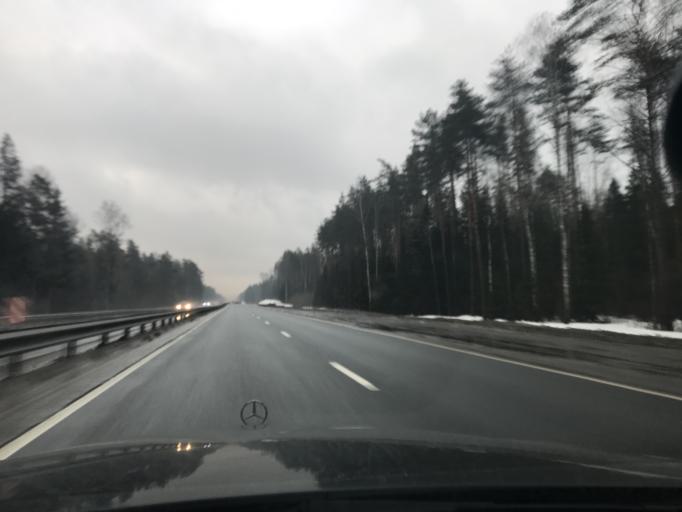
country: RU
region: Vladimir
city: Melekhovo
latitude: 56.2135
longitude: 41.3547
